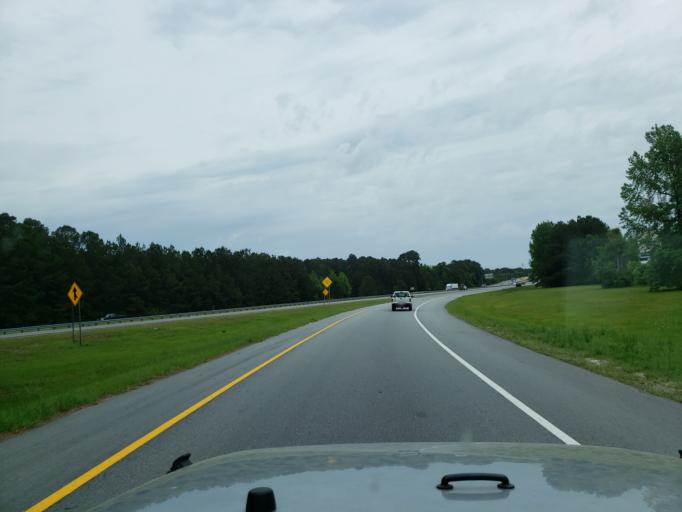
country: US
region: Georgia
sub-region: Chatham County
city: Port Wentworth
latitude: 32.1684
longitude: -81.2130
